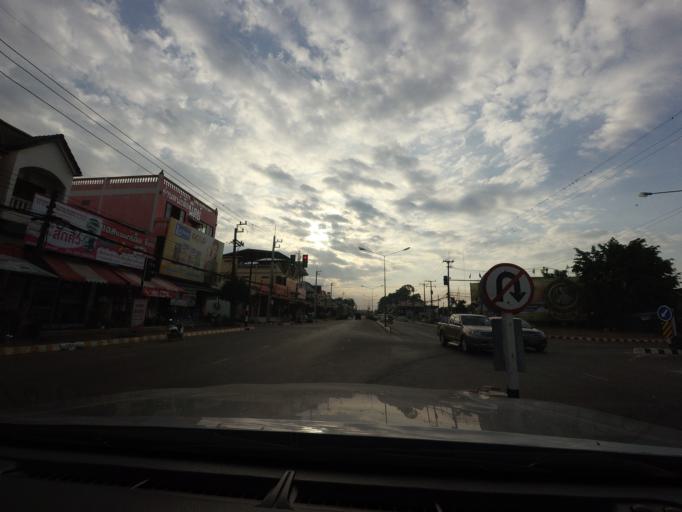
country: TH
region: Phitsanulok
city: Noen Maprang
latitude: 16.5671
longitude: 100.6353
